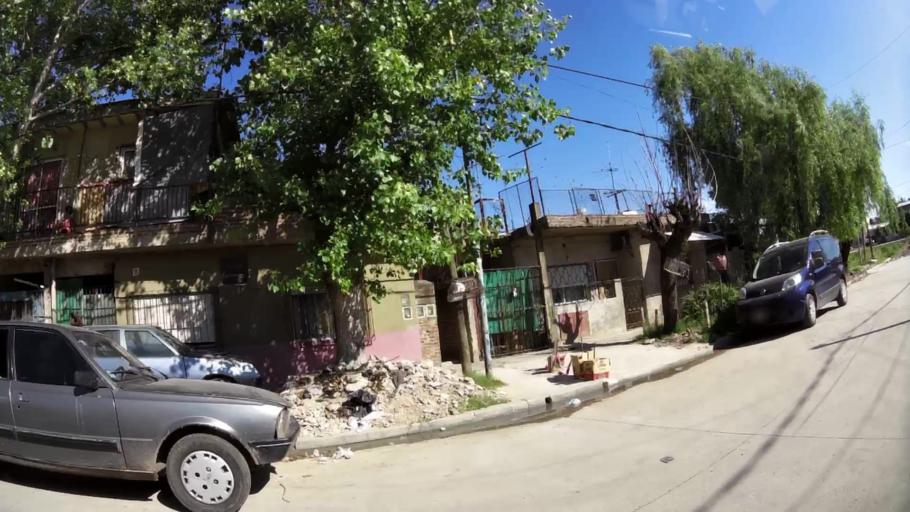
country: AR
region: Buenos Aires
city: Hurlingham
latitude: -34.5432
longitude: -58.5934
